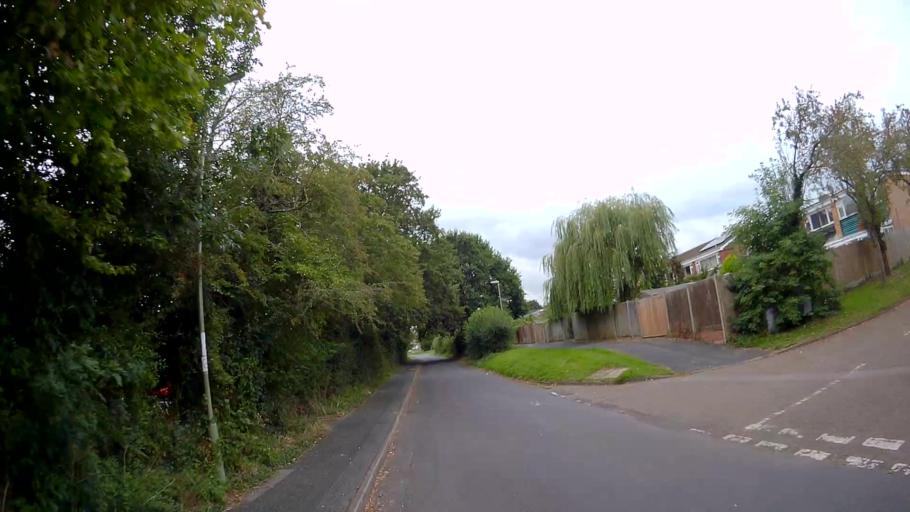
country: GB
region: England
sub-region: Hampshire
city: Basingstoke
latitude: 51.2529
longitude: -1.0991
